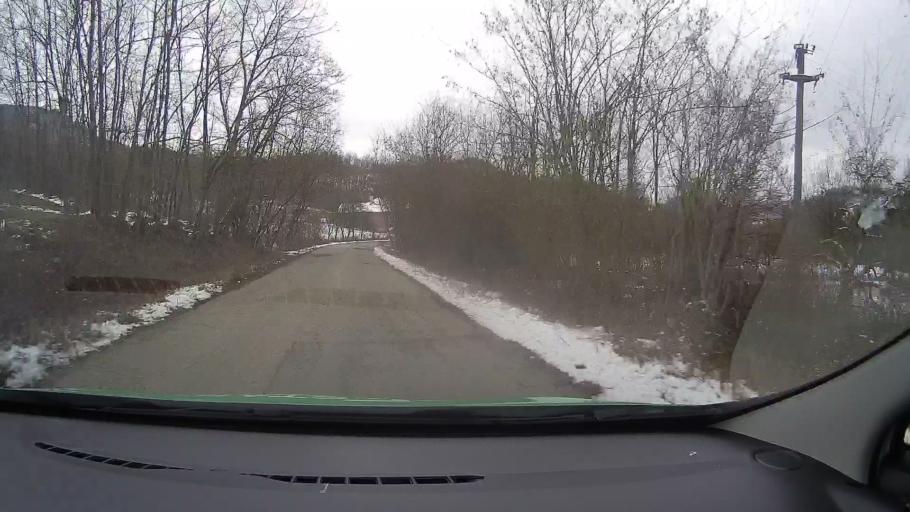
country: RO
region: Hunedoara
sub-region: Comuna Balsa
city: Balsa
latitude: 46.0354
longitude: 23.0806
